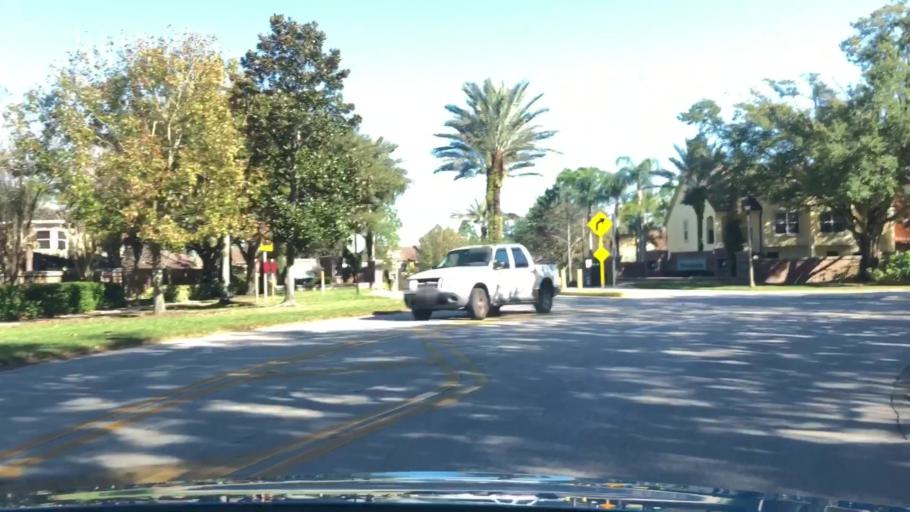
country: US
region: Florida
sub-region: Orange County
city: Eatonville
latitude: 28.6327
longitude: -81.3833
